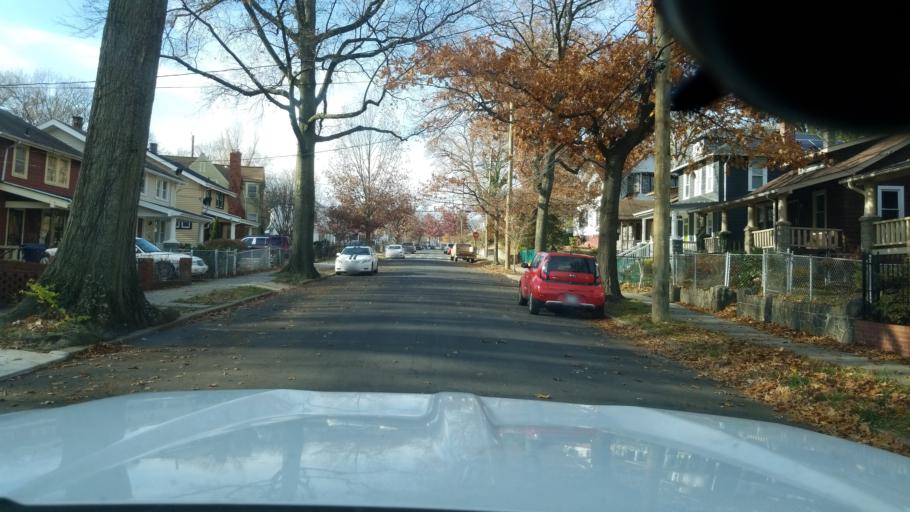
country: US
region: Maryland
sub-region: Prince George's County
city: Mount Rainier
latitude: 38.9313
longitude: -76.9664
